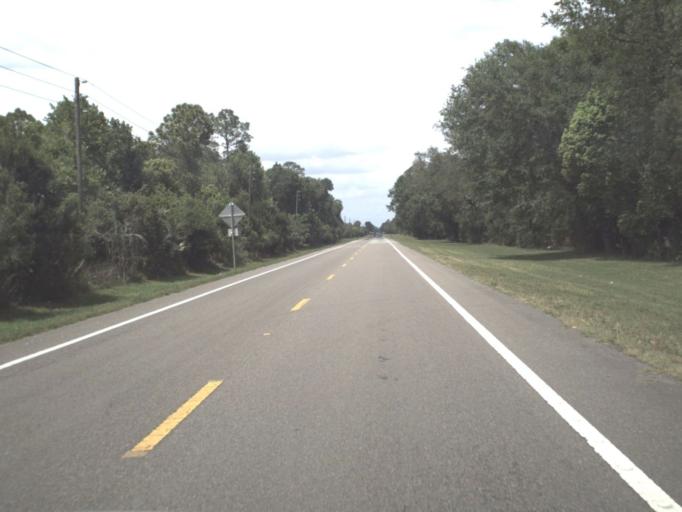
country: US
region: Florida
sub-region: Flagler County
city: Bunnell
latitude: 29.3317
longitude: -81.3106
